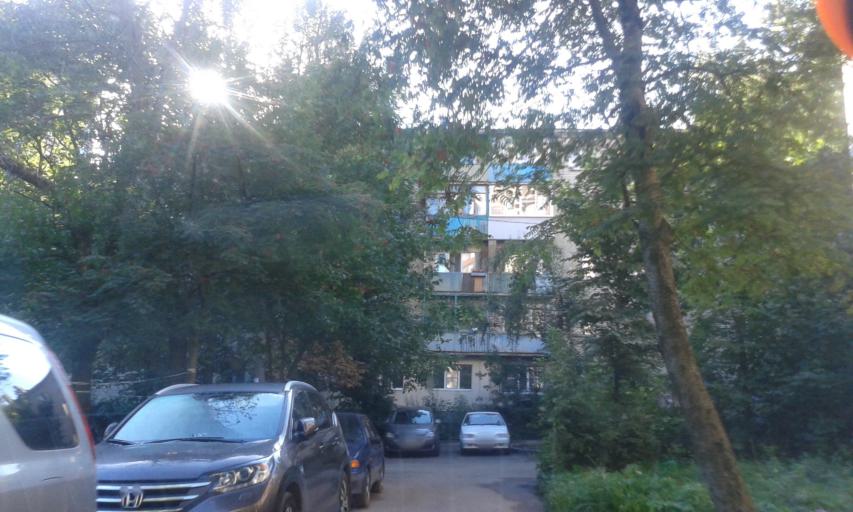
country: RU
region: Tula
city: Tula
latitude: 54.1872
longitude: 37.5963
